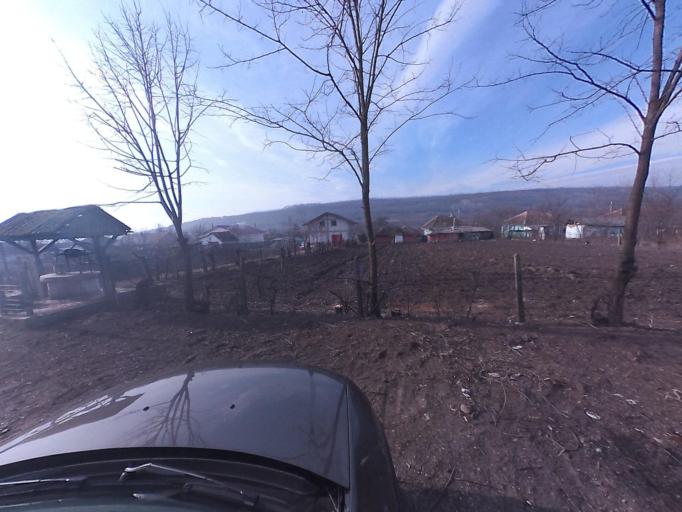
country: RO
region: Vaslui
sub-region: Comuna Solesti
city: Solesti
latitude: 46.8086
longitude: 27.7815
